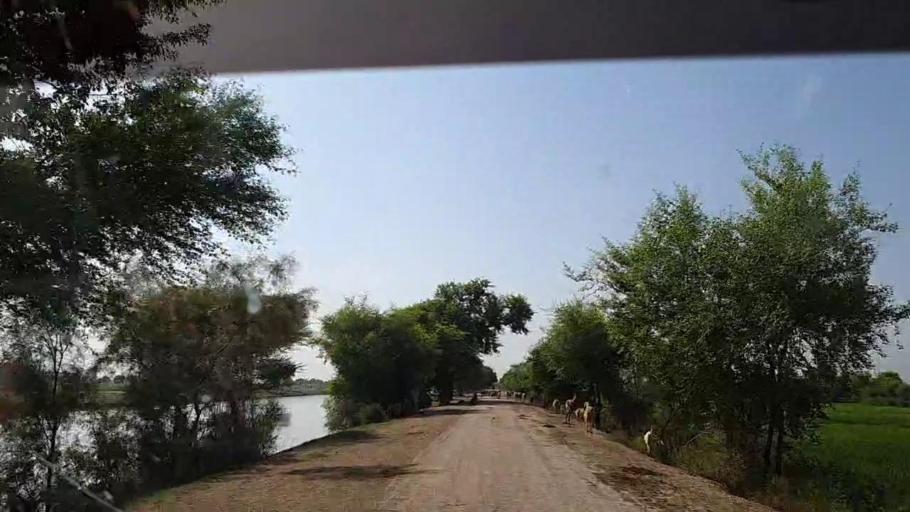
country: PK
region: Sindh
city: Ghauspur
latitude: 28.1925
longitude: 69.0549
